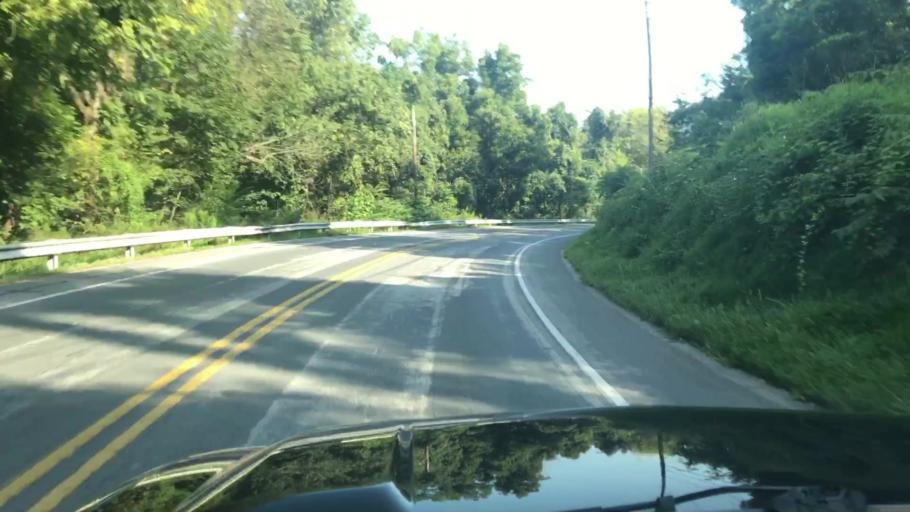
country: US
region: Pennsylvania
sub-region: York County
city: Valley Green
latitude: 40.1633
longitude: -76.8181
